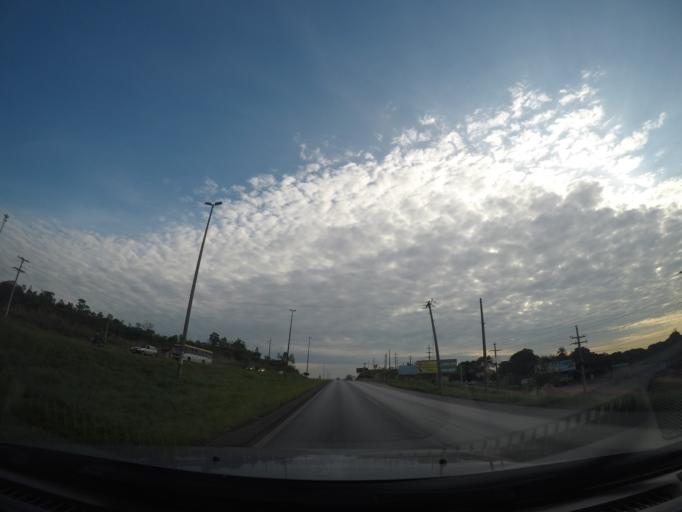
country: BR
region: Goias
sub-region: Planaltina
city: Planaltina
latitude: -15.6206
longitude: -47.7156
